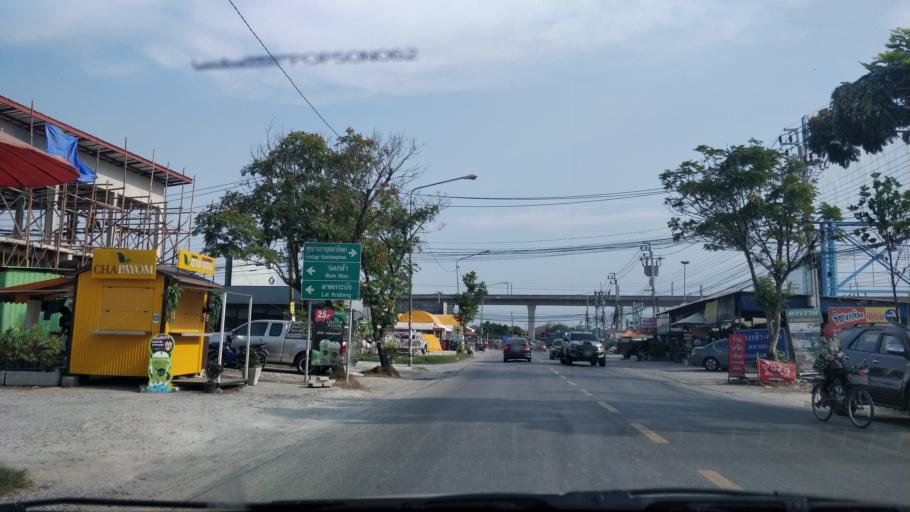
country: TH
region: Bangkok
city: Saphan Sung
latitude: 13.7329
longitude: 100.7163
